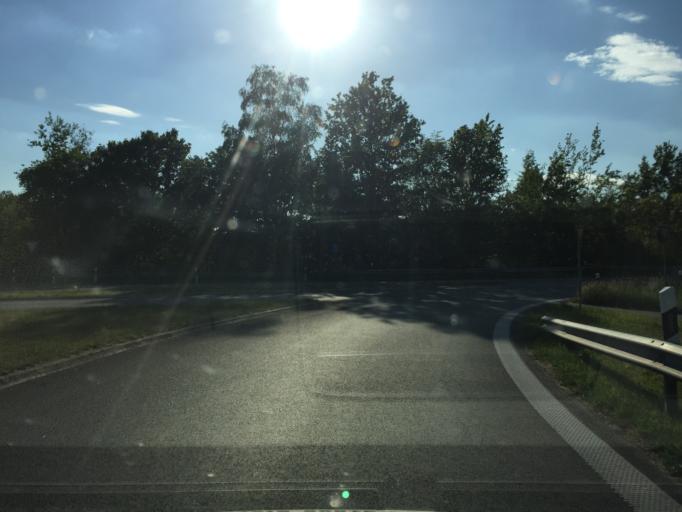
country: DE
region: Lower Saxony
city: Rastede
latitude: 53.2430
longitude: 8.1749
